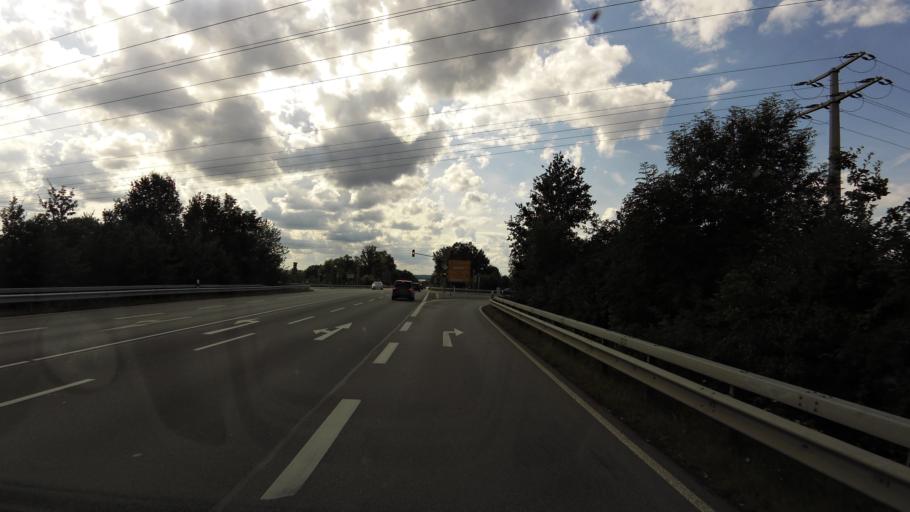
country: DE
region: Bavaria
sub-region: Upper Palatinate
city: Cham
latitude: 49.2134
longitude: 12.6780
